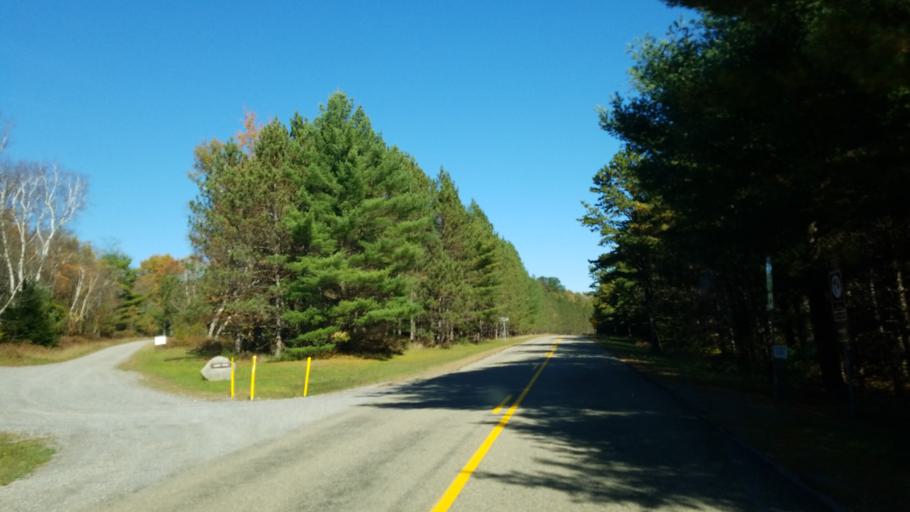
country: US
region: Pennsylvania
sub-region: Clearfield County
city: Shiloh
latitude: 41.2650
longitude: -78.2783
